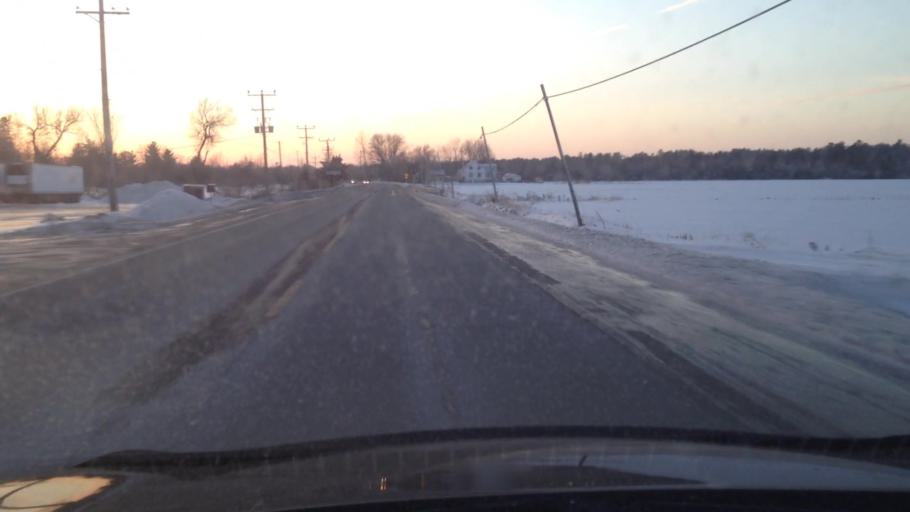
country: CA
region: Quebec
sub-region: Laurentides
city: Sainte-Sophie
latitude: 45.8345
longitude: -73.8629
